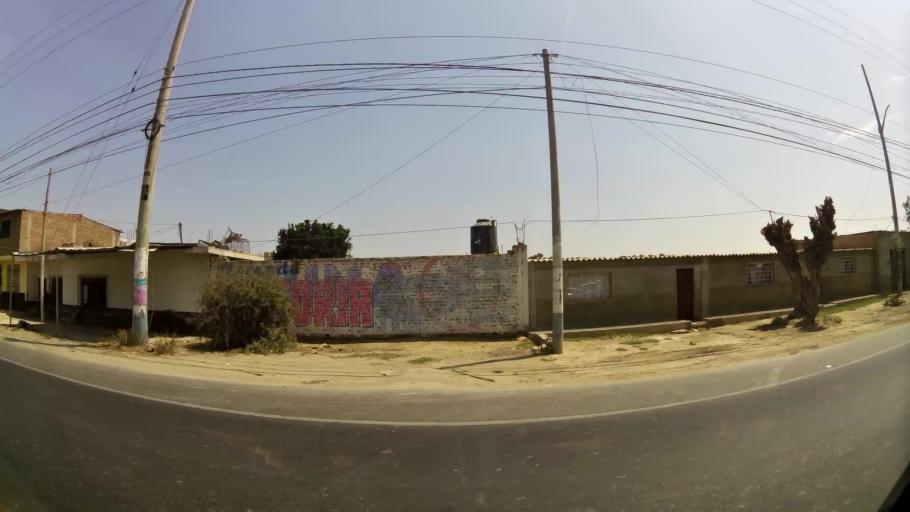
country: PE
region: La Libertad
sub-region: Chepen
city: Chepen
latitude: -7.2076
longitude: -79.4271
